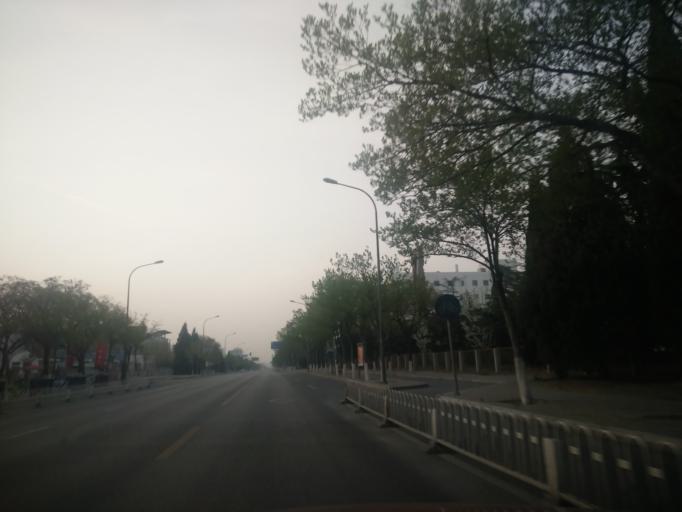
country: CN
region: Beijing
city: Jiugong
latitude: 39.7999
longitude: 116.5068
